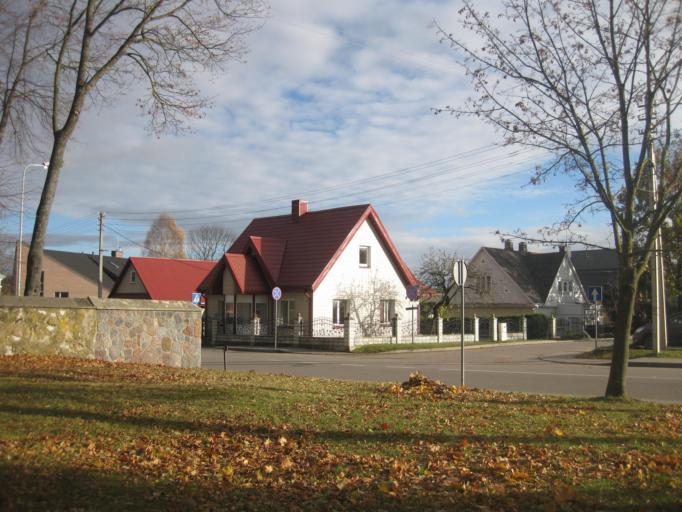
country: LT
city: Prienai
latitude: 54.6346
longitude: 23.9481
